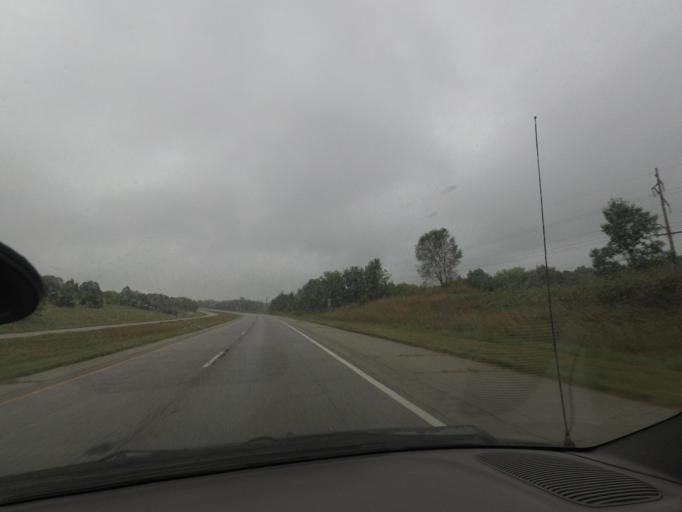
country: US
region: Illinois
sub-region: Pike County
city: Barry
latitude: 39.7115
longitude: -91.0598
